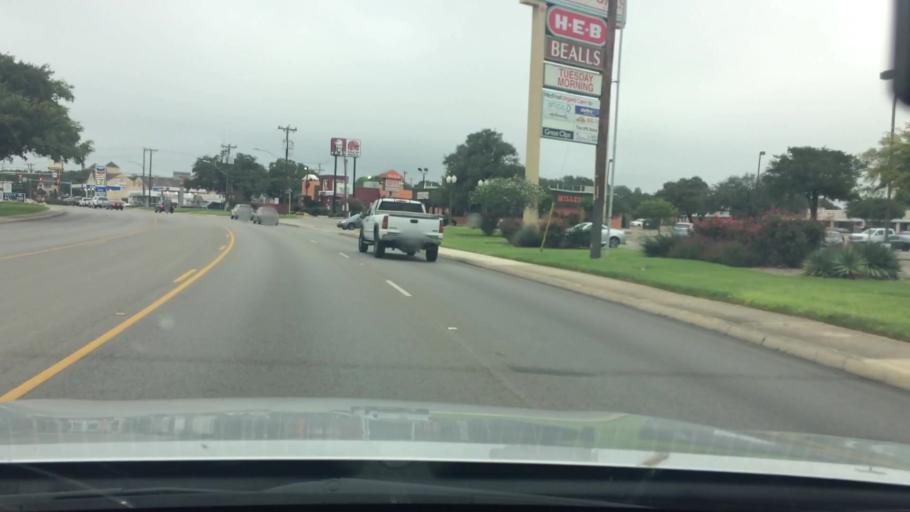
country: US
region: Texas
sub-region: Bexar County
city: Hollywood Park
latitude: 29.5768
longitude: -98.4406
